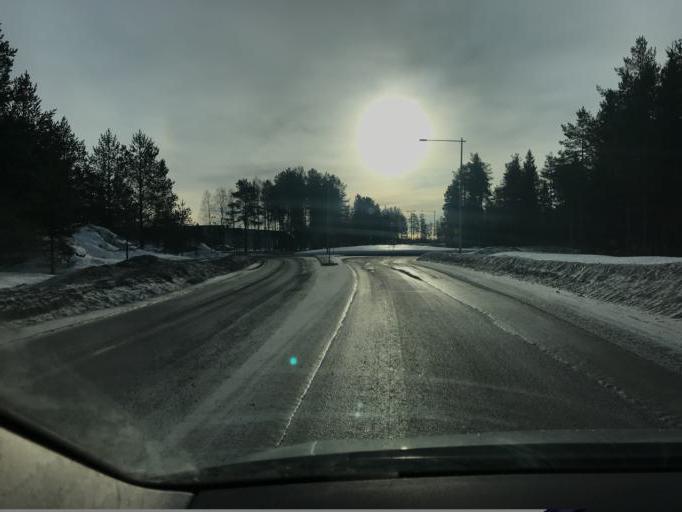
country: SE
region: Norrbotten
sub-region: Lulea Kommun
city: Gammelstad
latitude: 65.6174
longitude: 22.0391
